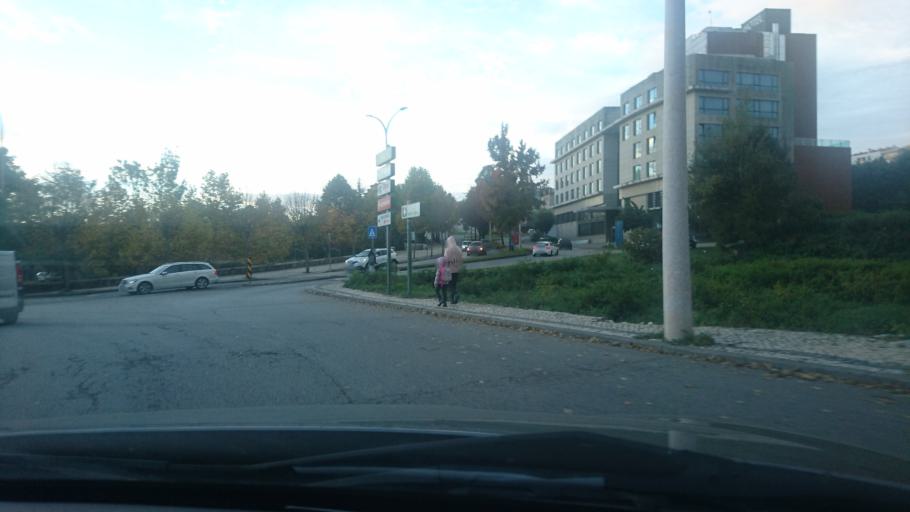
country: PT
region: Aveiro
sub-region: Sao Joao da Madeira
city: Sao Joao da Madeira
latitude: 40.8954
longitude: -8.4853
